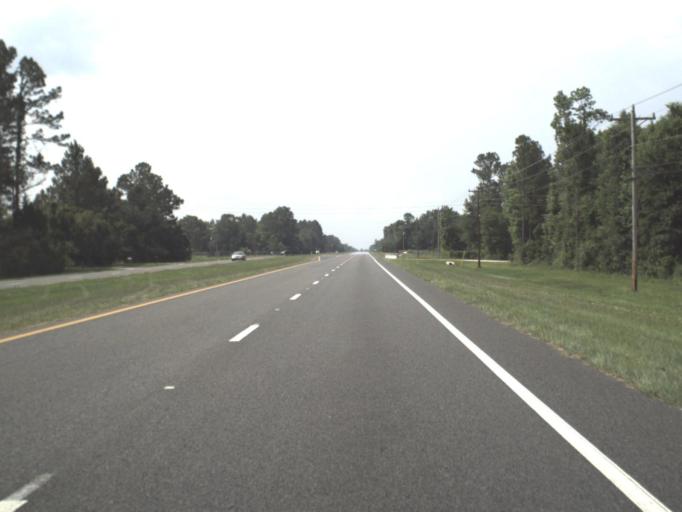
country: US
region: Florida
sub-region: Clay County
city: Green Cove Springs
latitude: 29.8986
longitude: -81.6726
